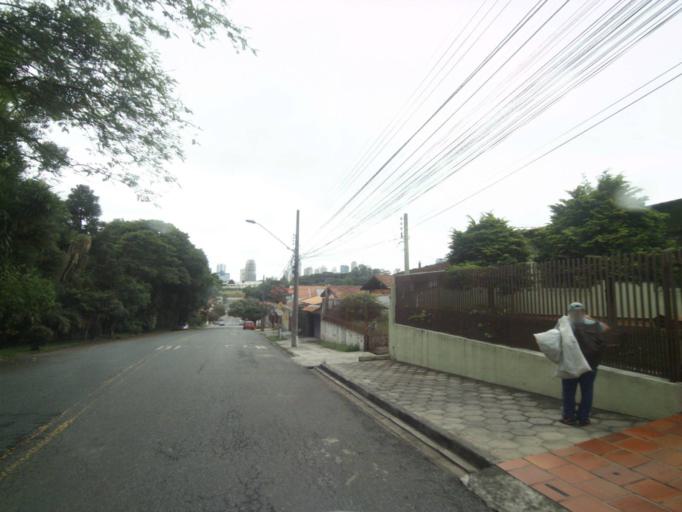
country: BR
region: Parana
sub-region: Curitiba
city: Curitiba
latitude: -25.4271
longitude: -49.3415
